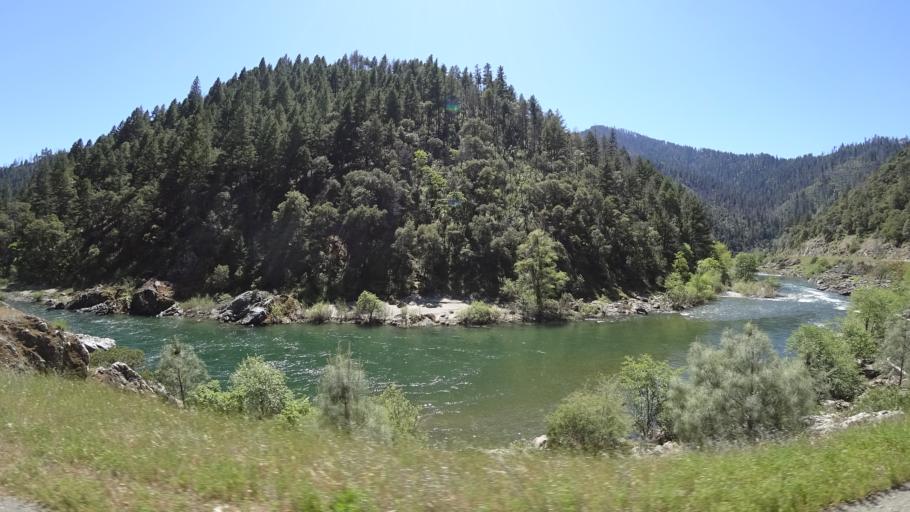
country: US
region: California
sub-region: Trinity County
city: Hayfork
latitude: 40.7677
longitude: -123.2952
